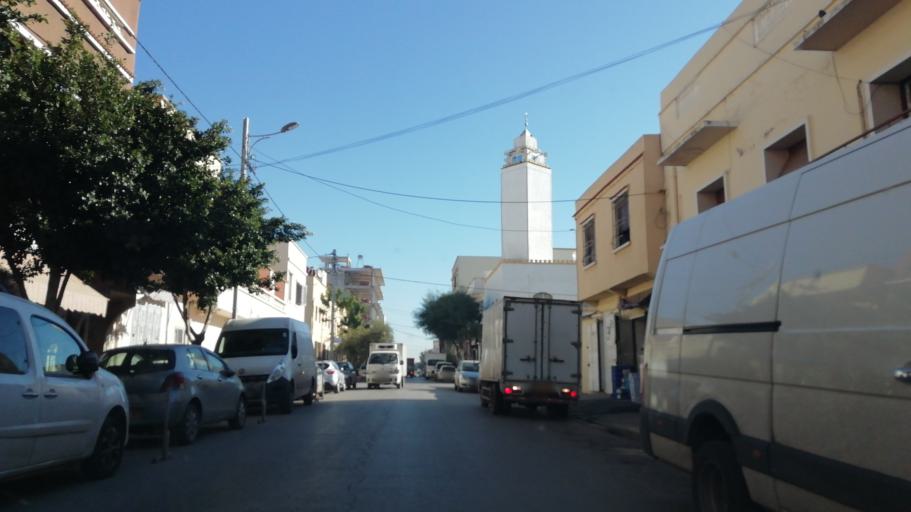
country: DZ
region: Oran
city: Oran
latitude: 35.6776
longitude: -0.6521
